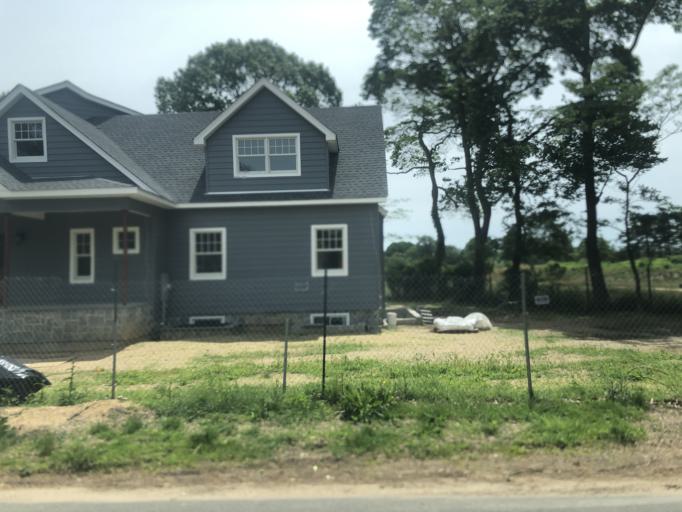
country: US
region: New York
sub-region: Nassau County
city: South Hempstead
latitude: 40.6819
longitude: -73.6280
